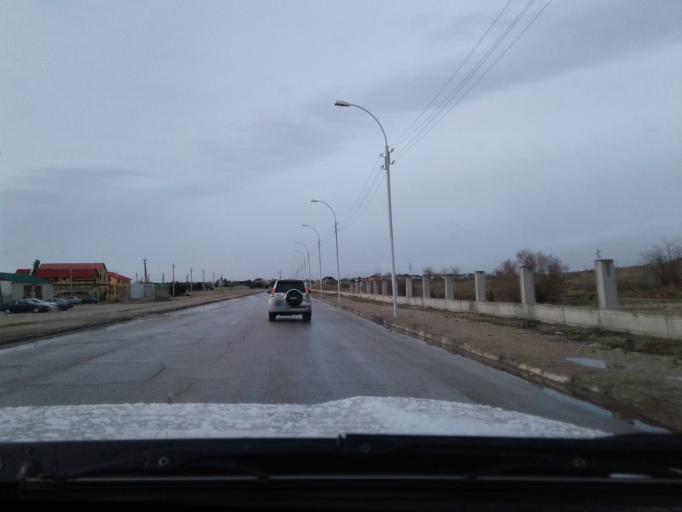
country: TM
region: Balkan
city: Balkanabat
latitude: 39.5284
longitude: 54.3602
